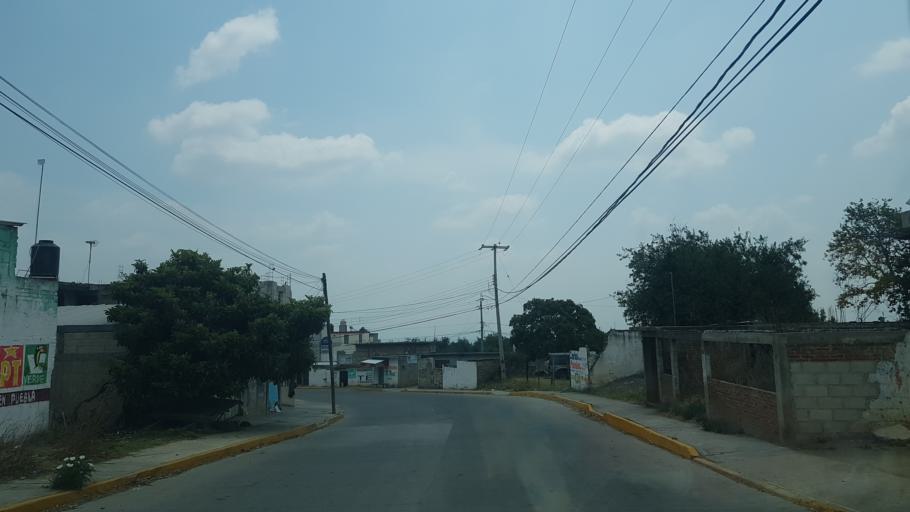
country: MX
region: Puebla
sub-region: Huejotzingo
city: San Juan Pancoac
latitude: 19.1384
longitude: -98.4405
